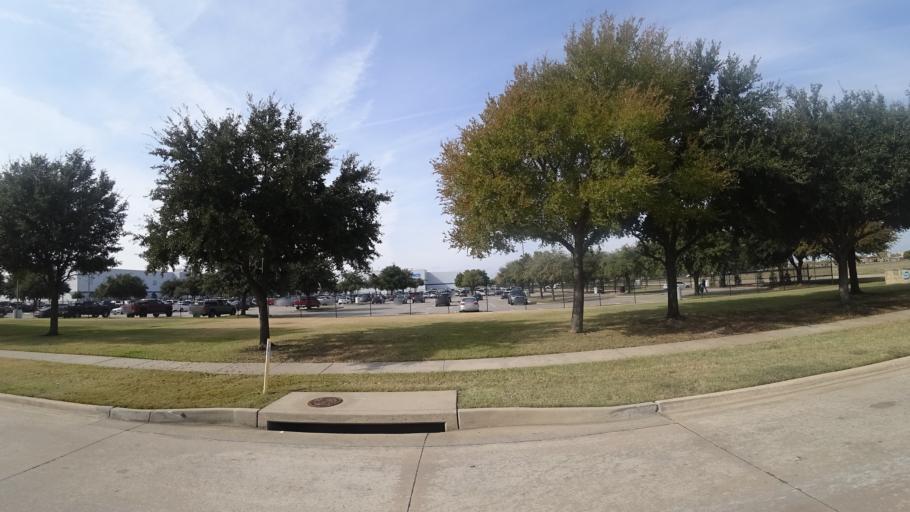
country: US
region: Texas
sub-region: Denton County
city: The Colony
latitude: 33.0651
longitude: -96.8713
